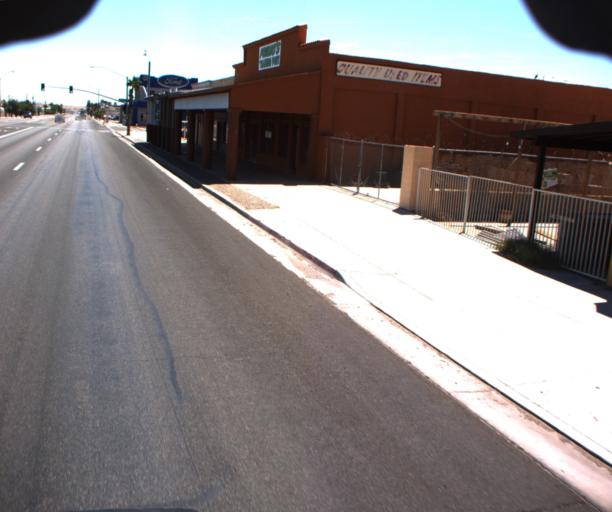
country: US
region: Arizona
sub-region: La Paz County
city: Parker
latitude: 34.1482
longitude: -114.2879
